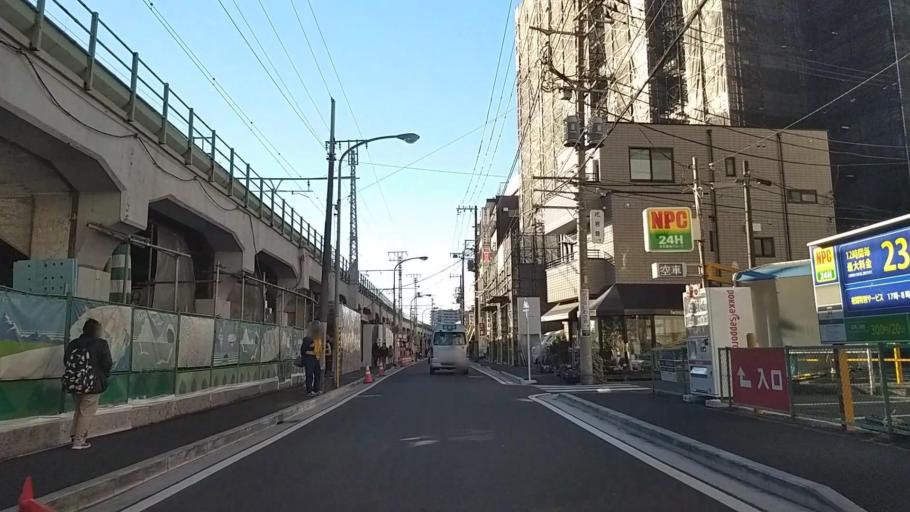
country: JP
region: Kanagawa
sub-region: Kawasaki-shi
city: Kawasaki
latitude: 35.5069
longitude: 139.6755
